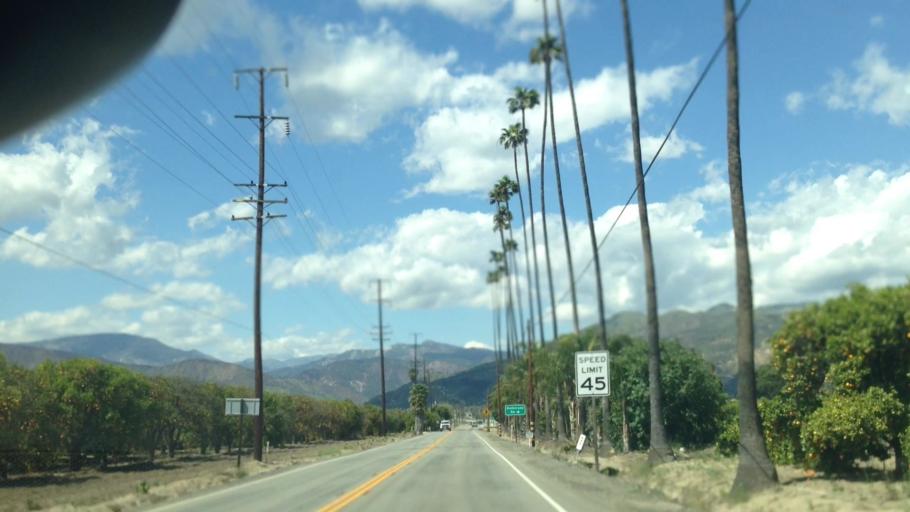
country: US
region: California
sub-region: Ventura County
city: Fillmore
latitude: 34.3755
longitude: -118.9157
